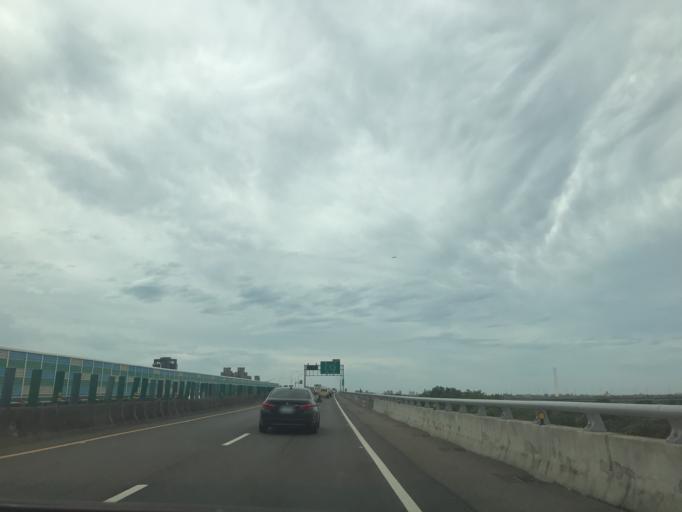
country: TW
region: Taiwan
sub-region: Hsinchu
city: Hsinchu
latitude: 24.8229
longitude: 120.9844
